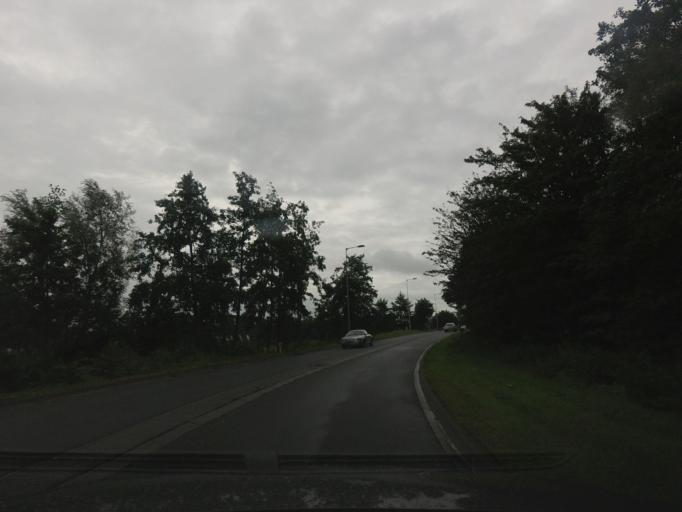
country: NL
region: North Holland
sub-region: Gemeente Haarlemmermeer
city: Hoofddorp
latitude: 52.3208
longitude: 4.6562
